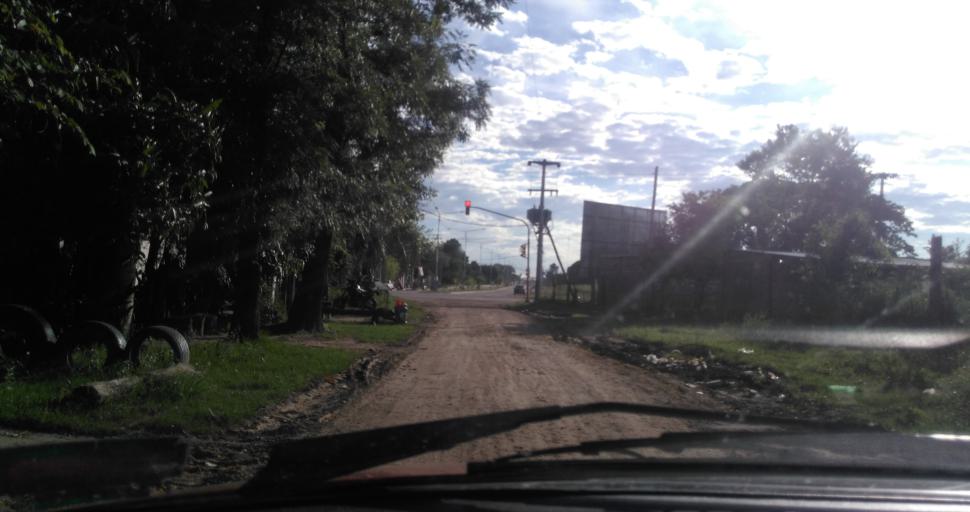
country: AR
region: Chaco
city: Fontana
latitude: -27.4115
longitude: -59.0302
